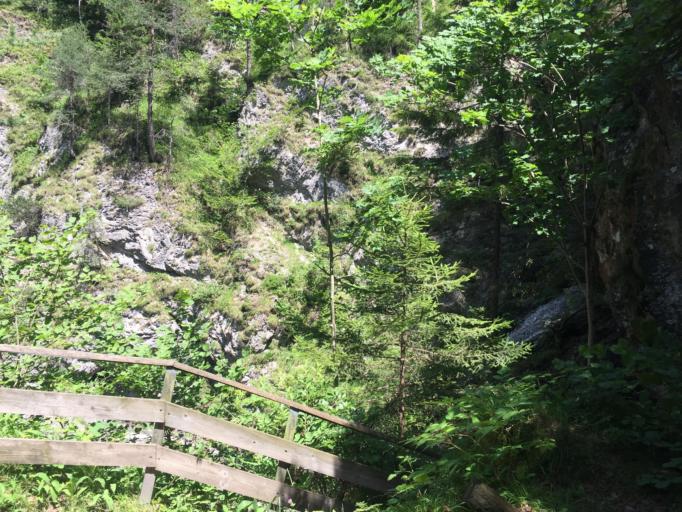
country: IT
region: Friuli Venezia Giulia
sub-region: Provincia di Udine
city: Tarvisio
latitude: 46.5071
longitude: 13.6030
